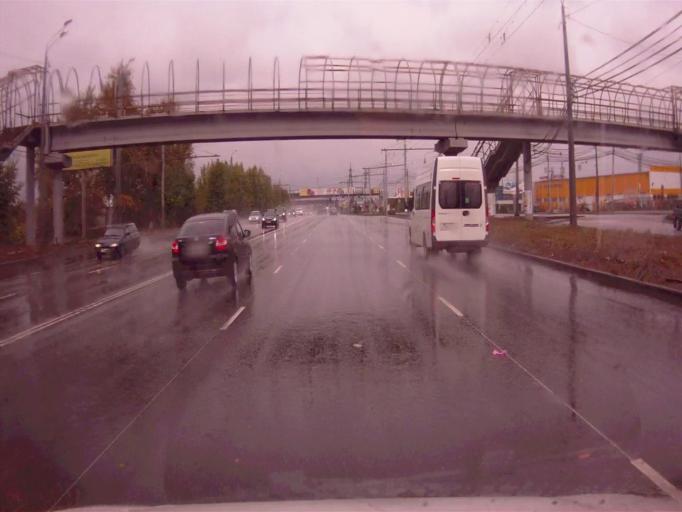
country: RU
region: Chelyabinsk
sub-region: Gorod Chelyabinsk
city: Chelyabinsk
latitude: 55.2008
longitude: 61.3858
